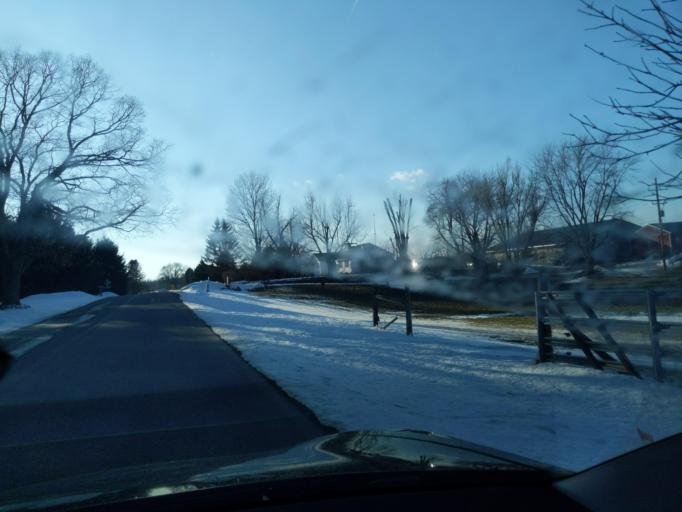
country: US
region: Michigan
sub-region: Ingham County
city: Stockbridge
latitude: 42.5194
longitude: -84.2355
